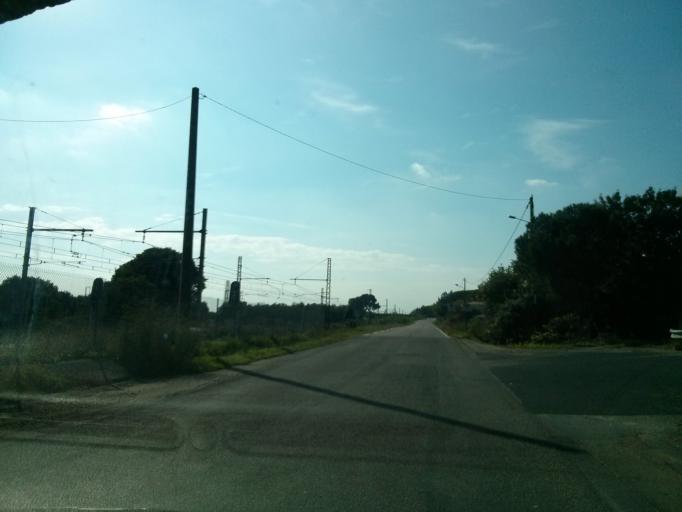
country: FR
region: Languedoc-Roussillon
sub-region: Departement du Gard
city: Gallargues-le-Montueux
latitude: 43.7214
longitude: 4.1815
